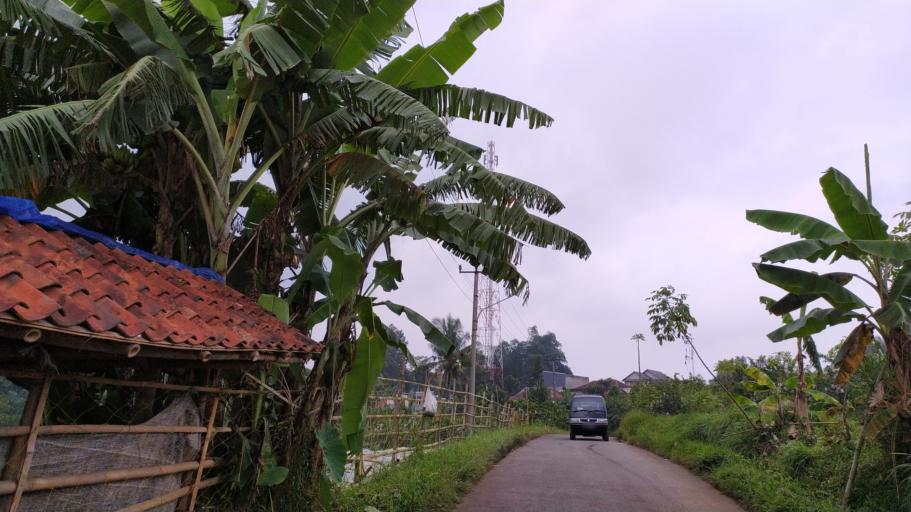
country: ID
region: West Java
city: Ciampea
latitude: -6.6410
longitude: 106.7070
